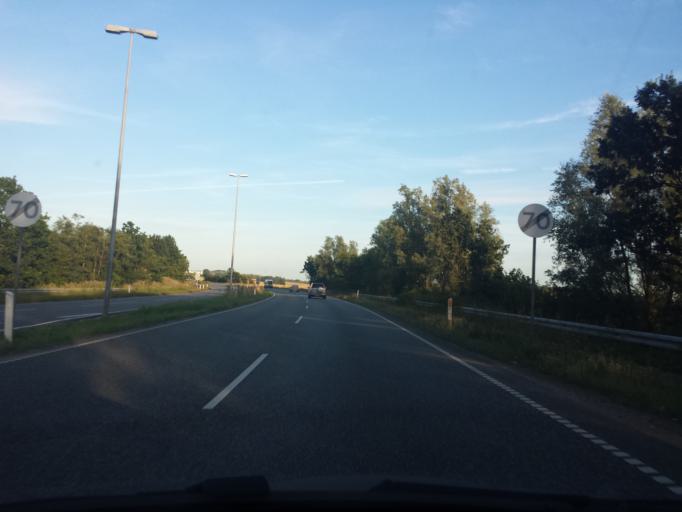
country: DK
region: Capital Region
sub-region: Egedal Kommune
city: Vekso
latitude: 55.7523
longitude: 12.2521
